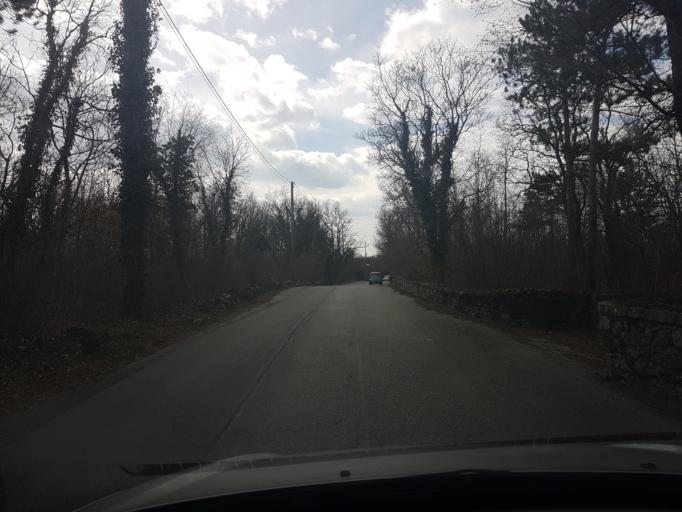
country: IT
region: Friuli Venezia Giulia
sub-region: Provincia di Trieste
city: Santa Croce
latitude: 45.7574
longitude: 13.7118
